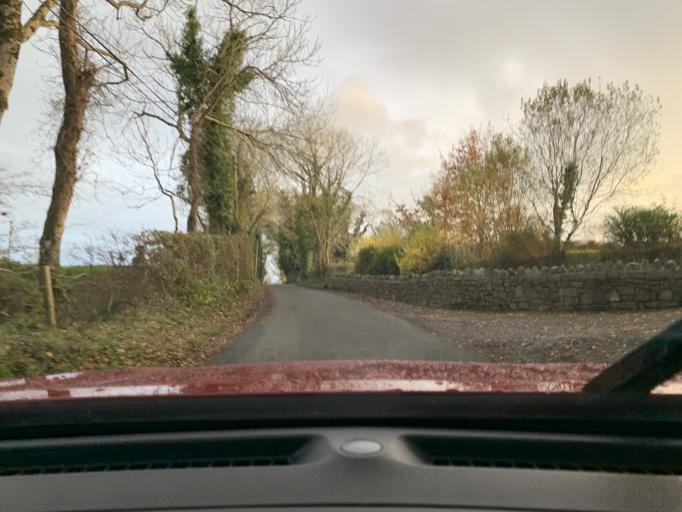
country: IE
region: Connaught
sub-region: Sligo
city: Sligo
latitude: 54.3010
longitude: -8.4921
